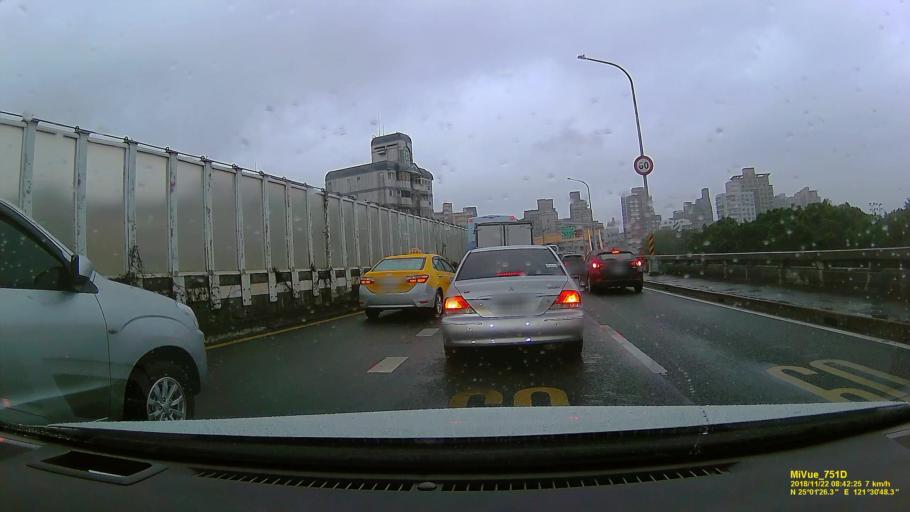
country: TW
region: Taipei
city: Taipei
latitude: 25.0240
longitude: 121.5134
